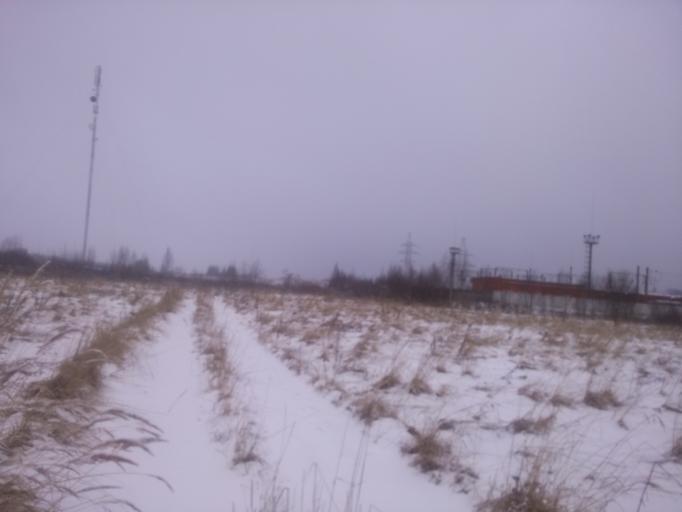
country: RU
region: Tverskaya
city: Likhoslavl'
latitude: 57.0632
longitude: 35.5584
